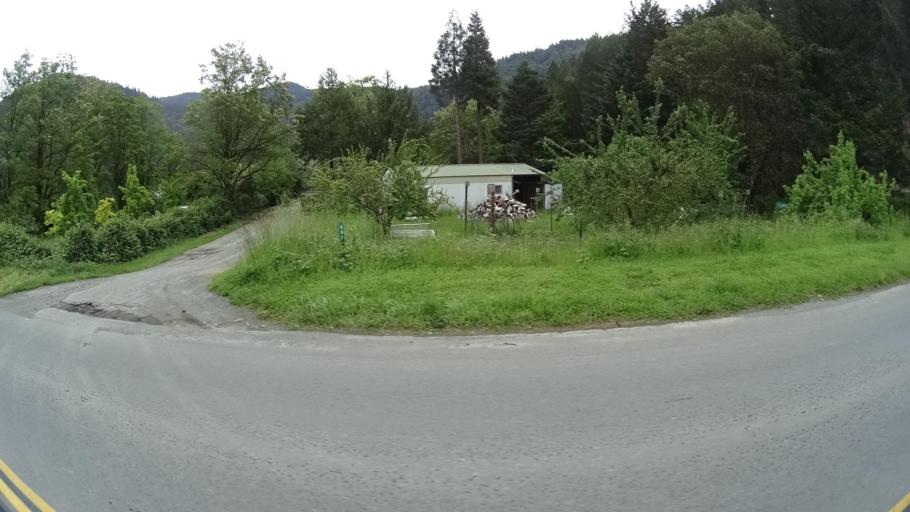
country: US
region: California
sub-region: Humboldt County
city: Willow Creek
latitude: 40.9425
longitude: -123.6227
